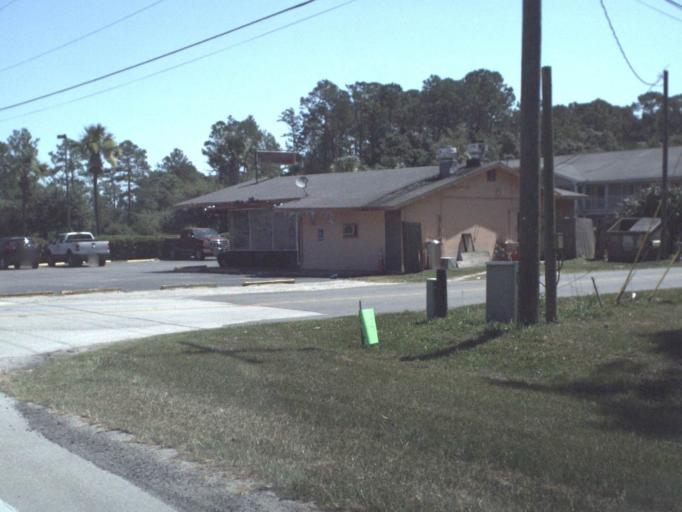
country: US
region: Florida
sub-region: Baker County
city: Macclenny
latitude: 30.2553
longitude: -82.1230
